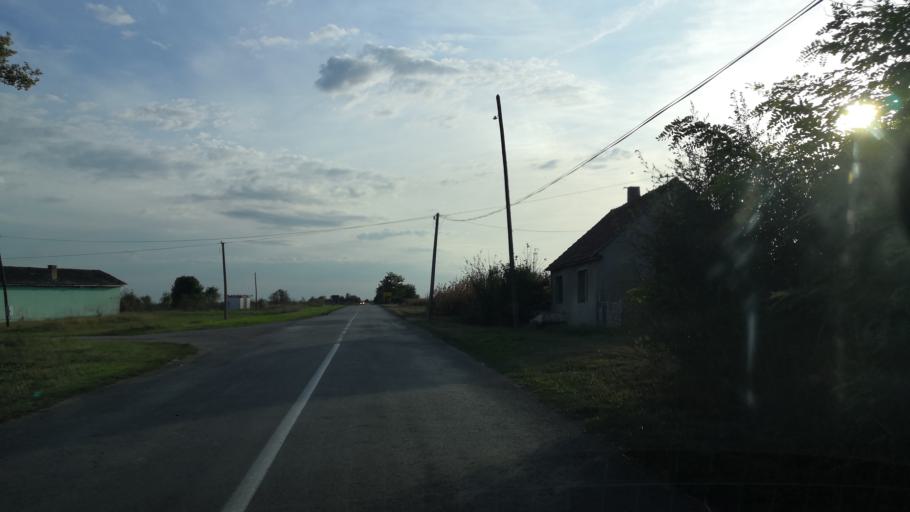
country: RS
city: Novi Karlovci
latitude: 45.0688
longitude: 20.1850
